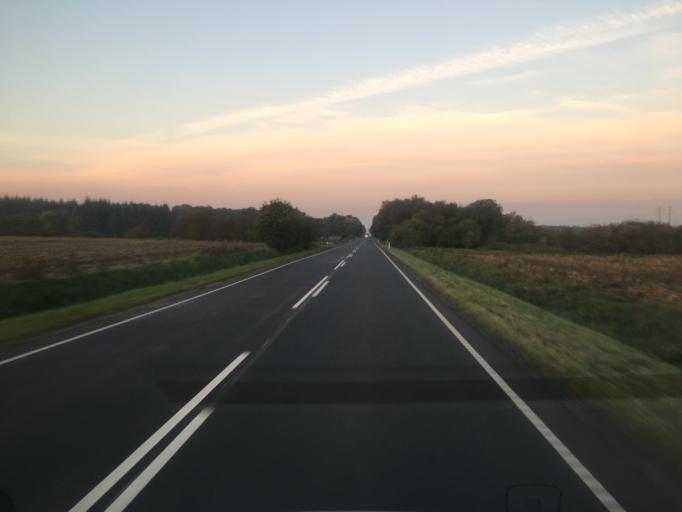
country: DK
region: South Denmark
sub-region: Aabenraa Kommune
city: Tinglev
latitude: 54.9741
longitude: 9.1296
